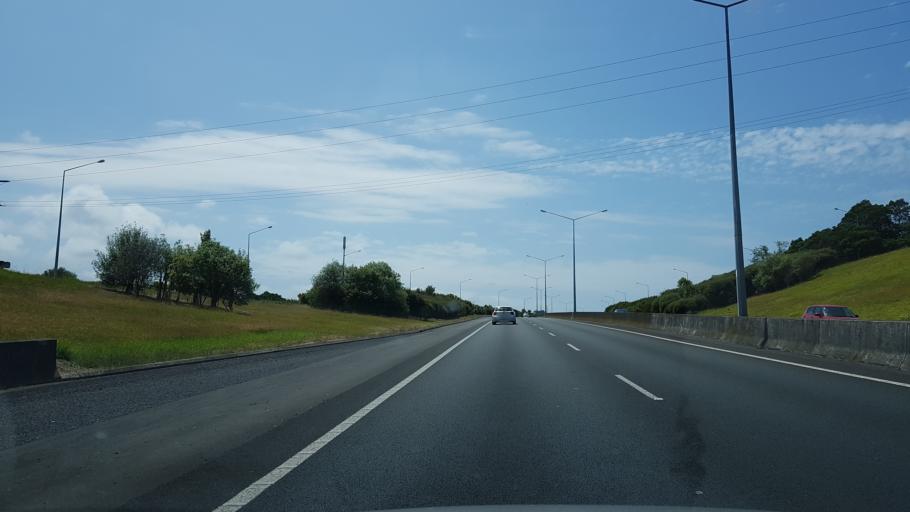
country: NZ
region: Auckland
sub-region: Auckland
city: North Shore
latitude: -36.7721
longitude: 174.6855
